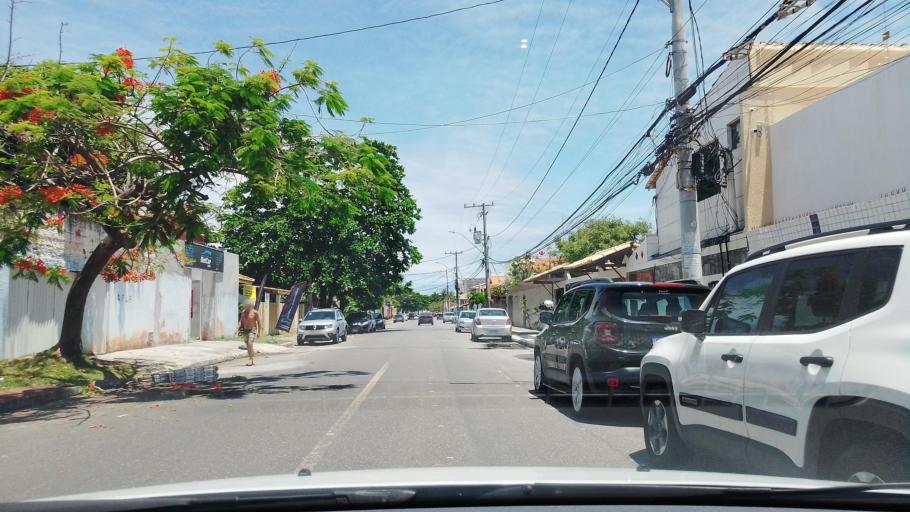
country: BR
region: Bahia
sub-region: Lauro De Freitas
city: Lauro de Freitas
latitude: -12.9378
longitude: -38.3323
